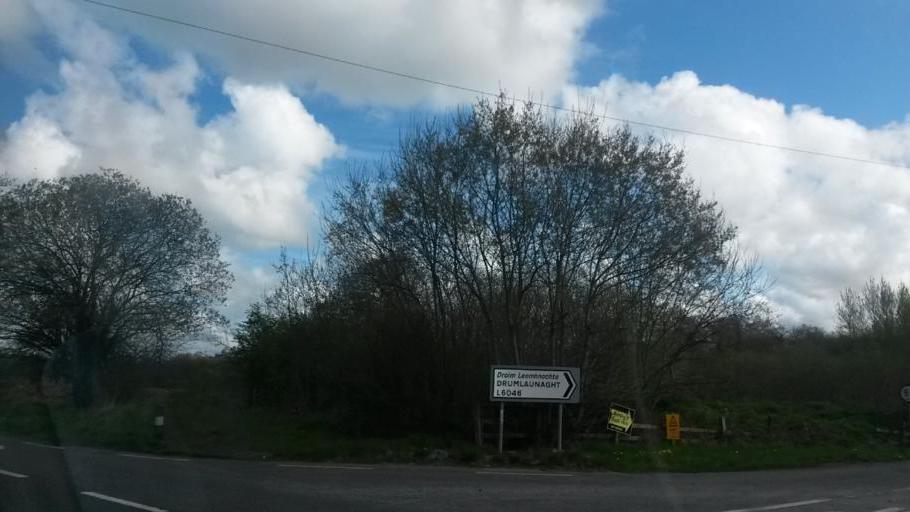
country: IE
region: Ulster
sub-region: An Cabhan
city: Cavan
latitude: 53.9757
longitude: -7.2470
